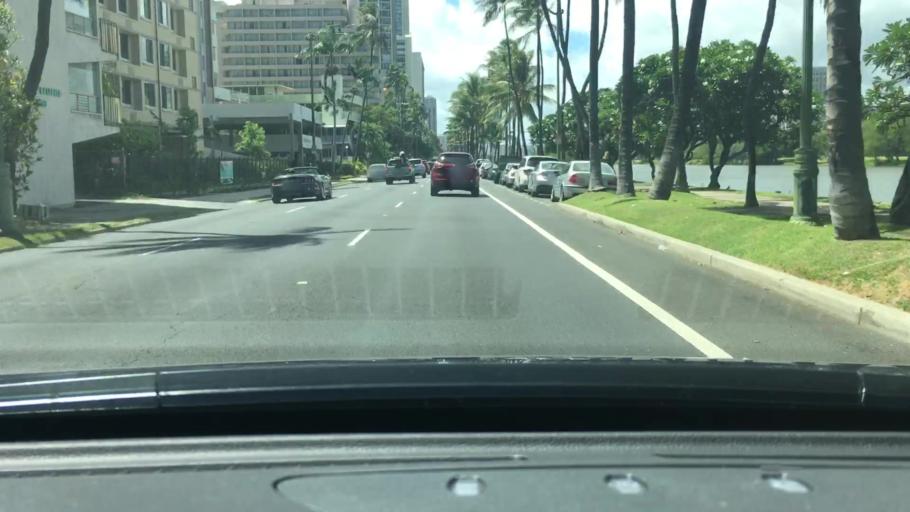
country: US
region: Hawaii
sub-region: Honolulu County
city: Honolulu
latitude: 21.2779
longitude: -157.8214
